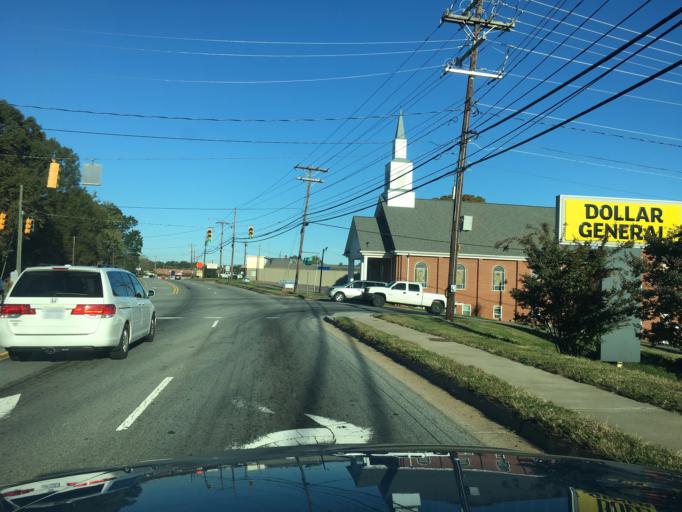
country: US
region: North Carolina
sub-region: Catawba County
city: Hickory
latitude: 35.7225
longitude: -81.3183
